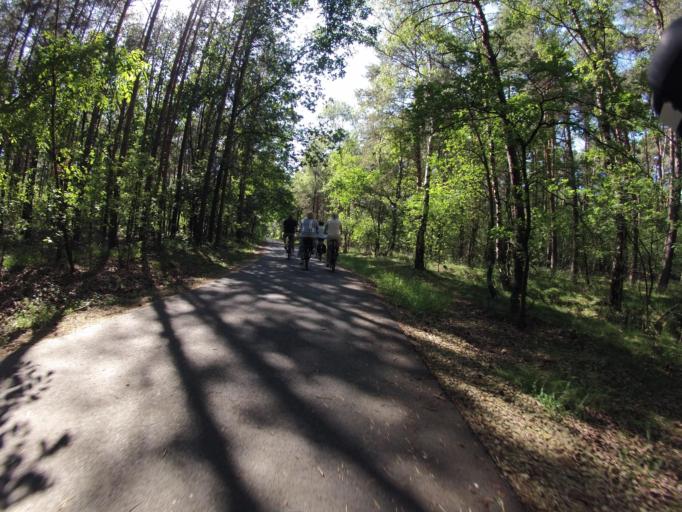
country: DE
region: North Rhine-Westphalia
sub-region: Regierungsbezirk Munster
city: Horstel
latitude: 52.2598
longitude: 7.5408
